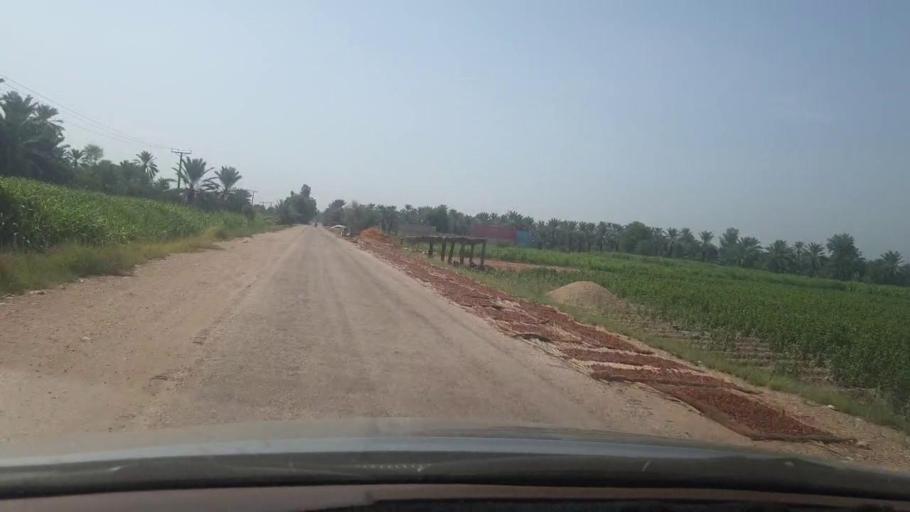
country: PK
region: Sindh
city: Ranipur
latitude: 27.2885
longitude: 68.5772
